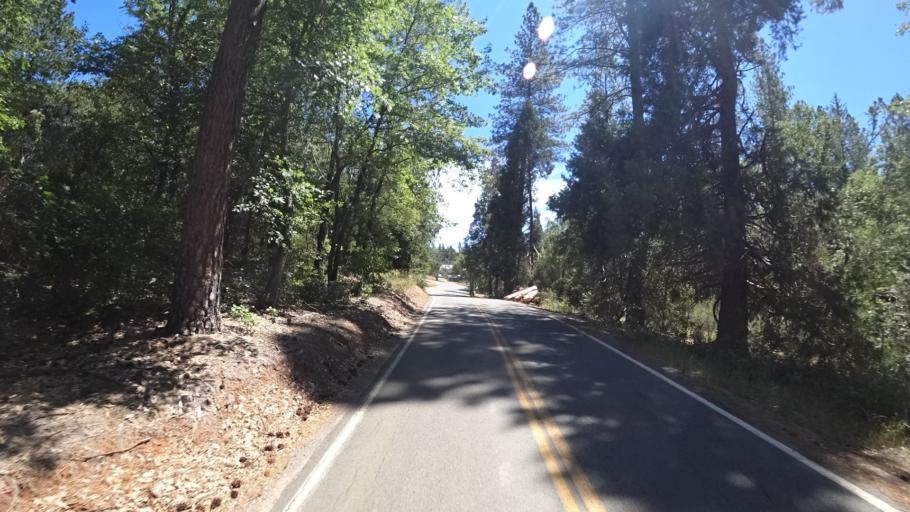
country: US
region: California
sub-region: Amador County
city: Pioneer
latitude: 38.3542
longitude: -120.5211
